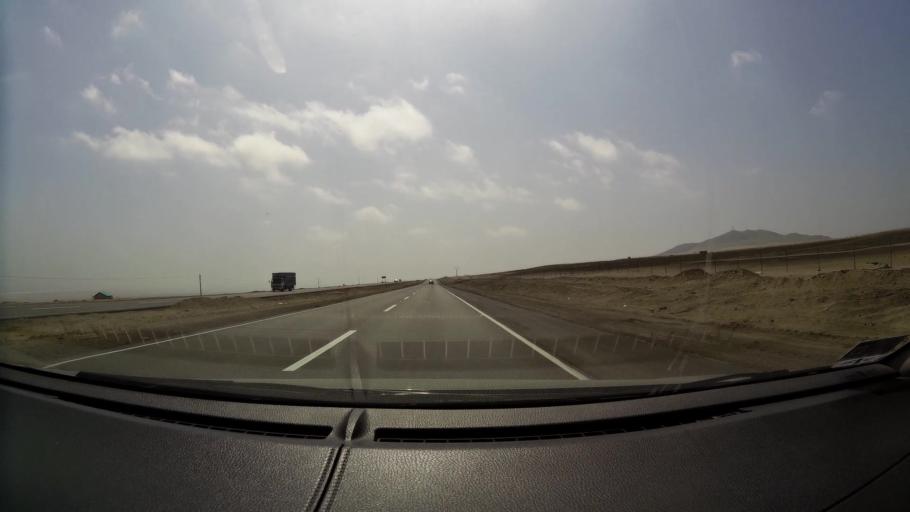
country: PE
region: Lima
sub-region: Provincia de Huaral
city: Huaral
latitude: -11.3538
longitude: -77.4539
